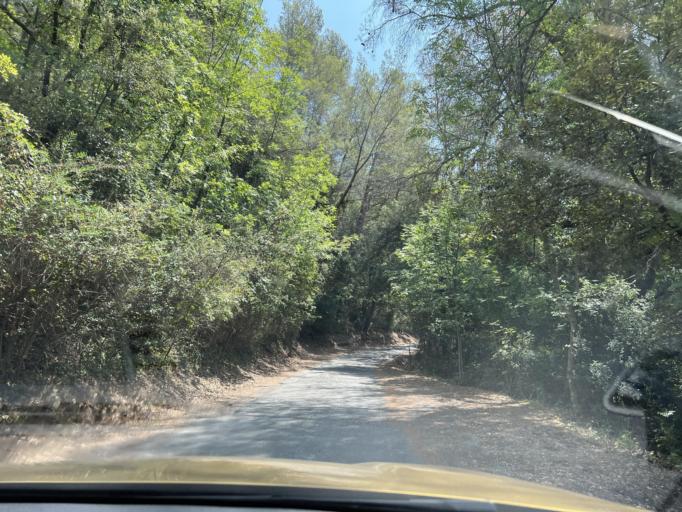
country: FR
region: Provence-Alpes-Cote d'Azur
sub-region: Departement des Alpes-Maritimes
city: Tourrettes-sur-Loup
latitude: 43.7049
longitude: 7.0321
